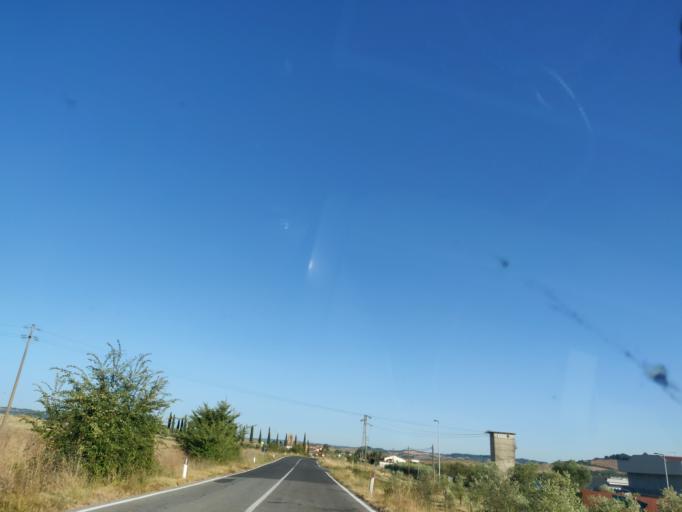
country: IT
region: Tuscany
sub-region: Provincia di Siena
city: Piancastagnaio
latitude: 42.8233
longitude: 11.7280
